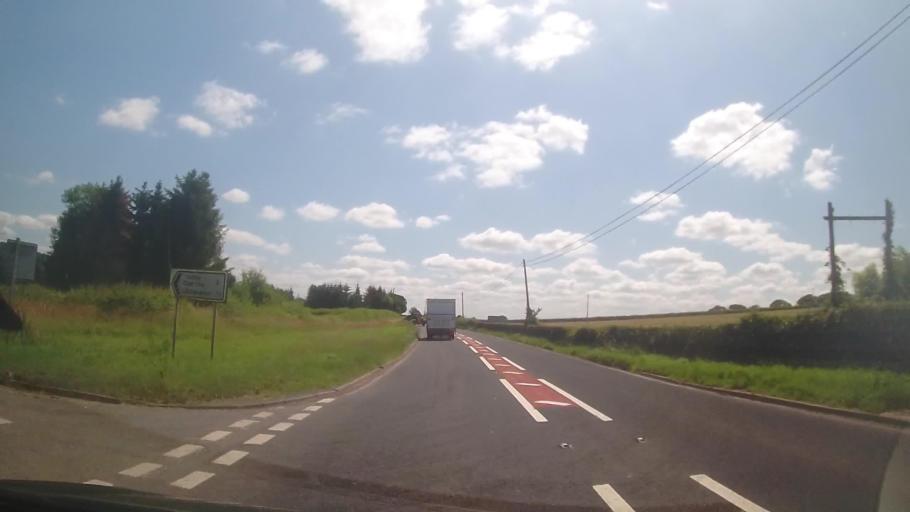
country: GB
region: England
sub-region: Herefordshire
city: Ocle Pychard
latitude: 52.1389
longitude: -2.6155
